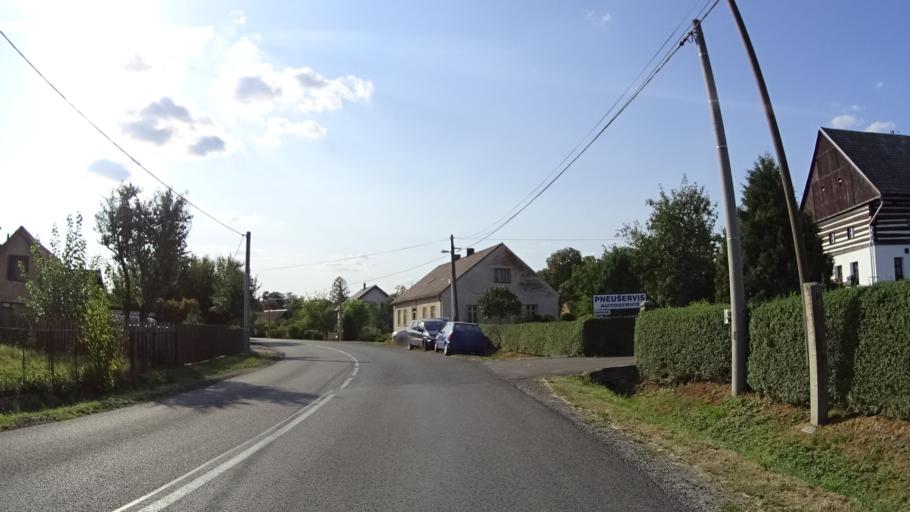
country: CZ
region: Central Bohemia
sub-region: Okres Mlada Boleslav
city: Zd'ar
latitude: 50.5432
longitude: 15.0908
